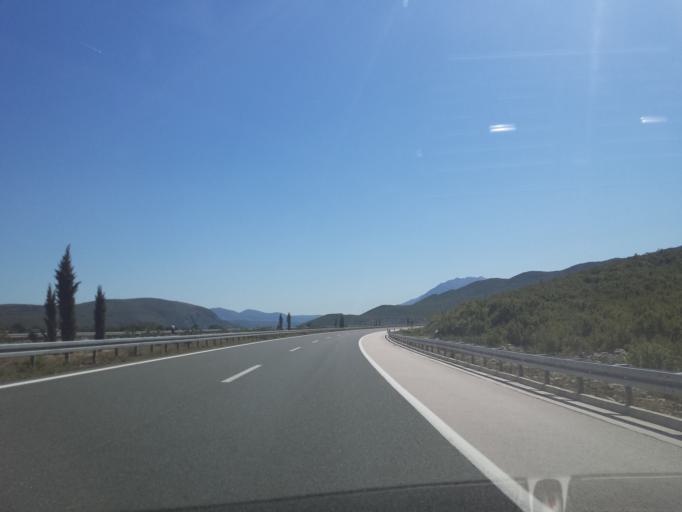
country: HR
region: Splitsko-Dalmatinska
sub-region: Grad Omis
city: Omis
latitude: 43.4917
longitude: 16.7946
